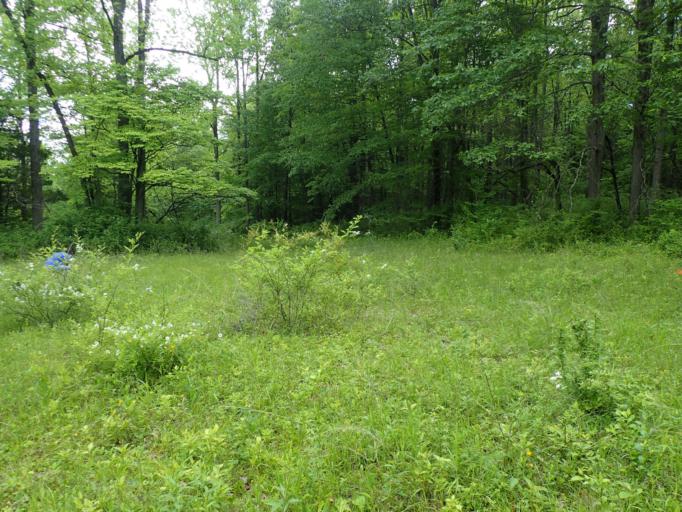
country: US
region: New Jersey
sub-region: Morris County
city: Morristown
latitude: 40.7811
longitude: -74.5372
